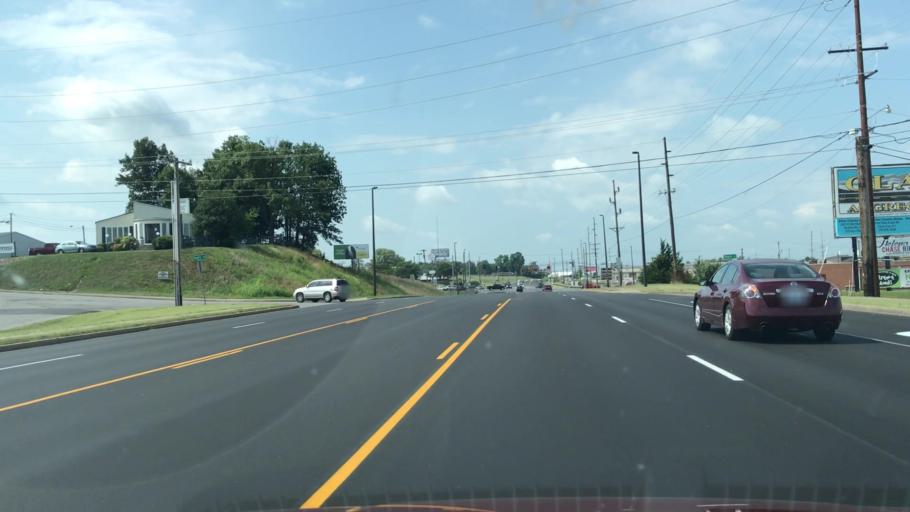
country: US
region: Kentucky
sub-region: Barren County
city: Glasgow
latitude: 37.0043
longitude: -85.9254
